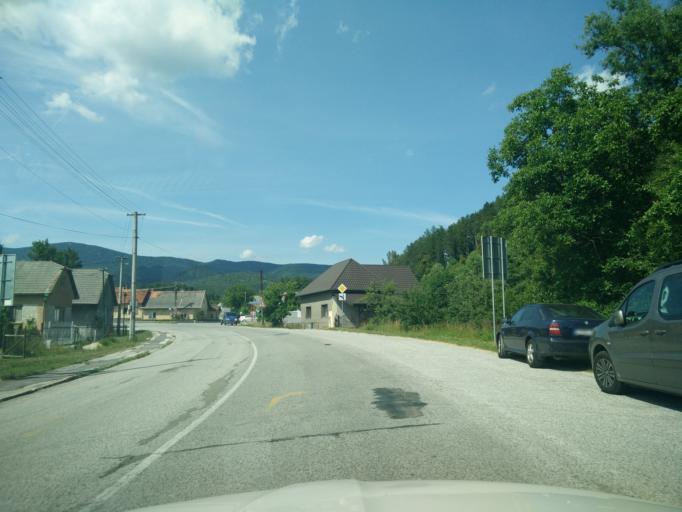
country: SK
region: Nitriansky
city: Prievidza
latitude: 48.9113
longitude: 18.6583
